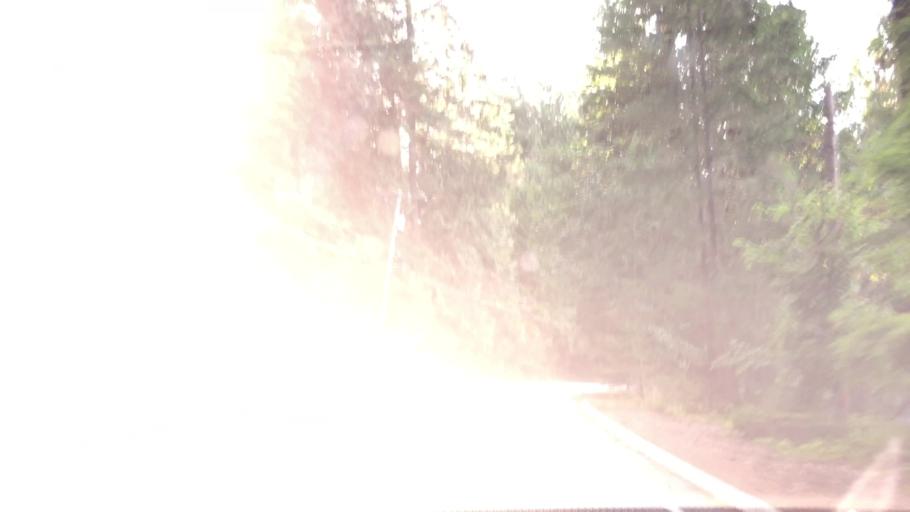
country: US
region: Washington
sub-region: King County
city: Woodinville
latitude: 47.7581
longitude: -122.1246
